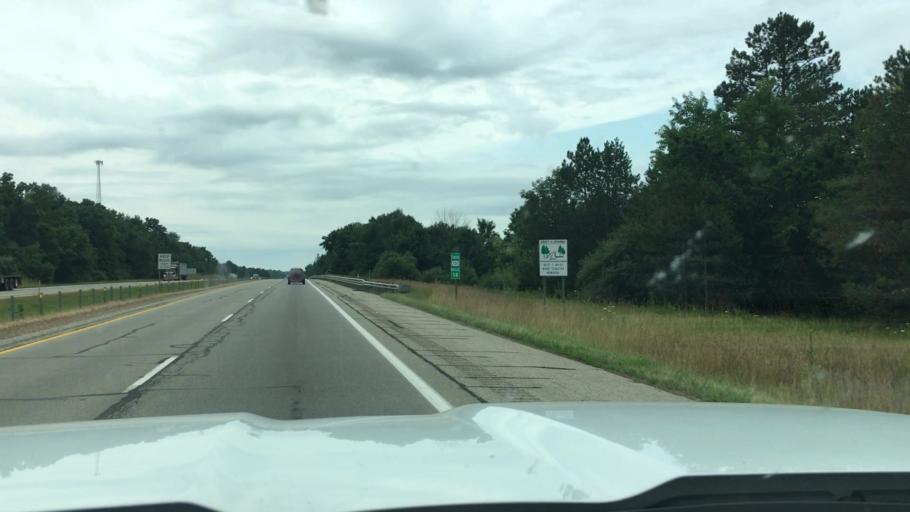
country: US
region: Michigan
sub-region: Allegan County
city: Wayland
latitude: 42.5809
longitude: -85.6629
